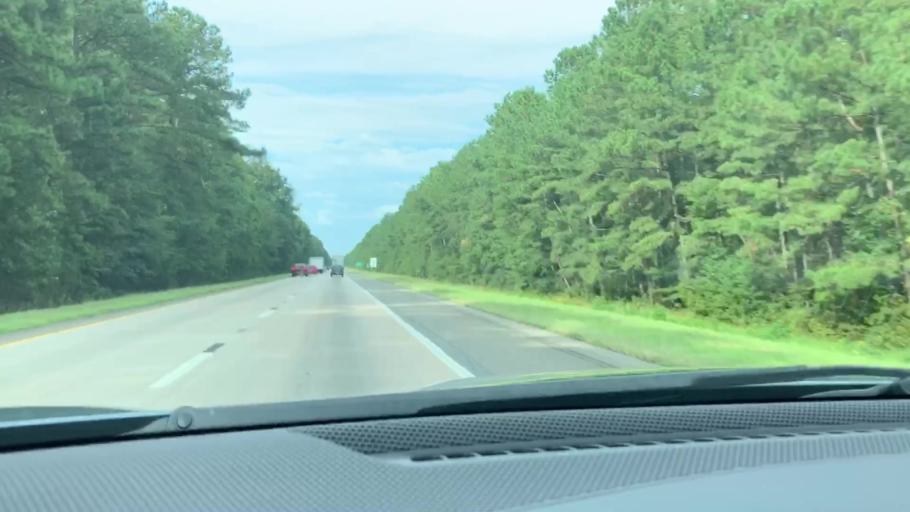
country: US
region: South Carolina
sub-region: Colleton County
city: Walterboro
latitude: 32.9795
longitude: -80.6740
